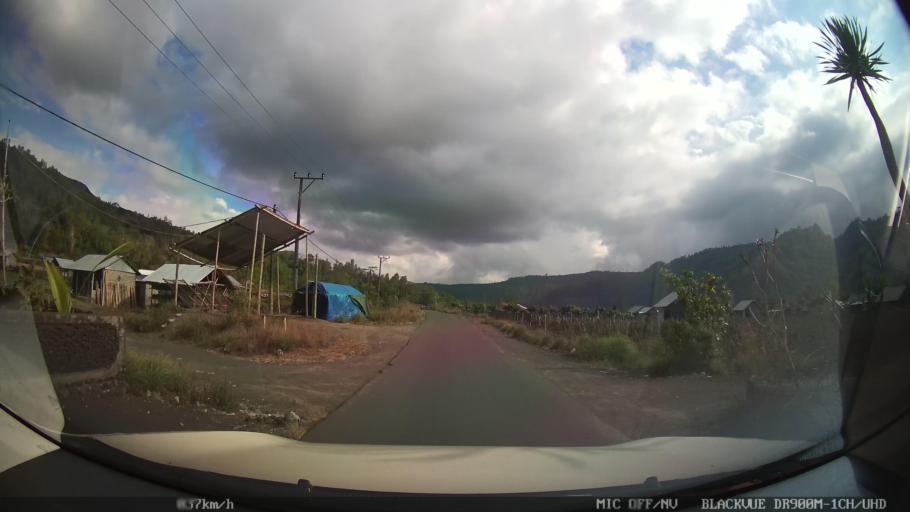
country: ID
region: Bali
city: Banjar Kedisan
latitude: -8.2258
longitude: 115.3595
